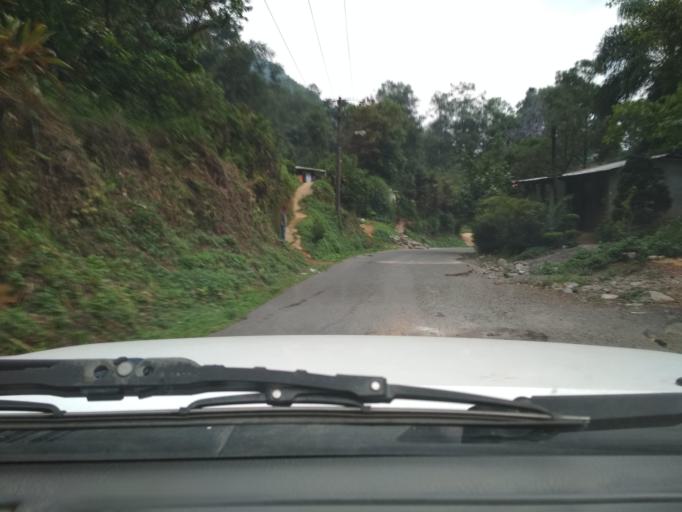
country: MX
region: Veracruz
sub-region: La Perla
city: Barrio de San Miguel
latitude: 18.9392
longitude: -97.1282
